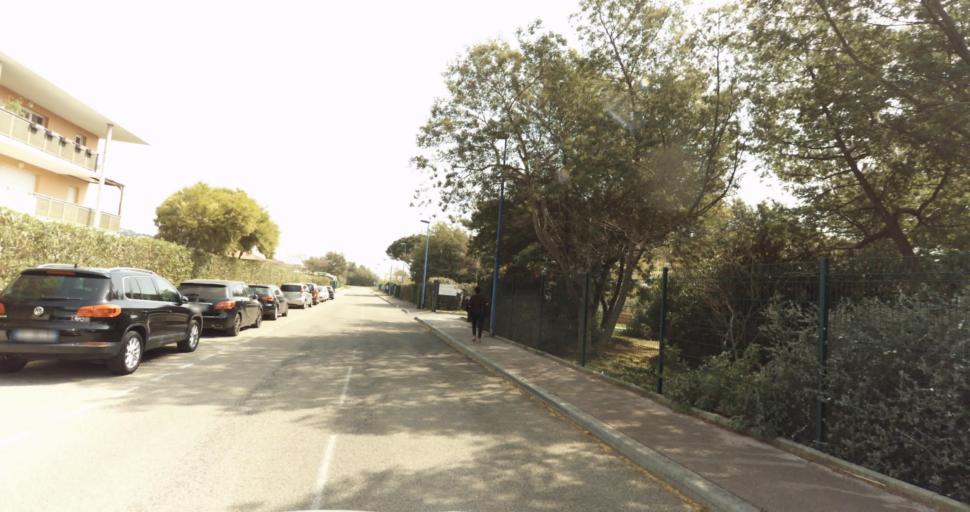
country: FR
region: Provence-Alpes-Cote d'Azur
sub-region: Departement du Var
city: Bormes-les-Mimosas
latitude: 43.1372
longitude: 6.3467
